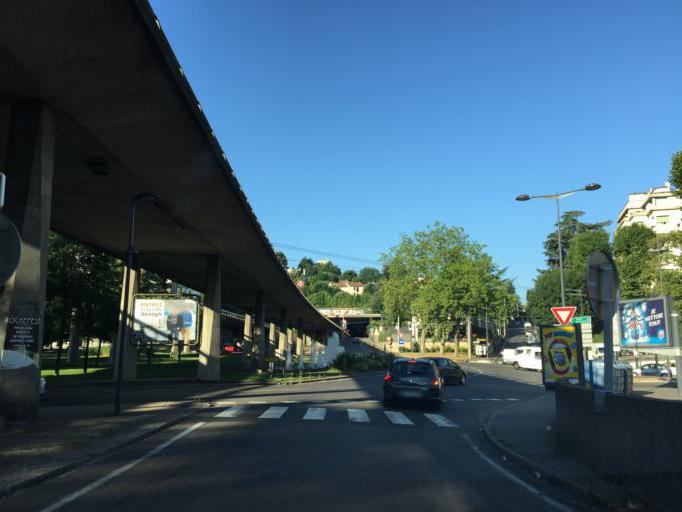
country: FR
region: Rhone-Alpes
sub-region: Departement de la Loire
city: Saint-Etienne
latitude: 45.4215
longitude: 4.4116
